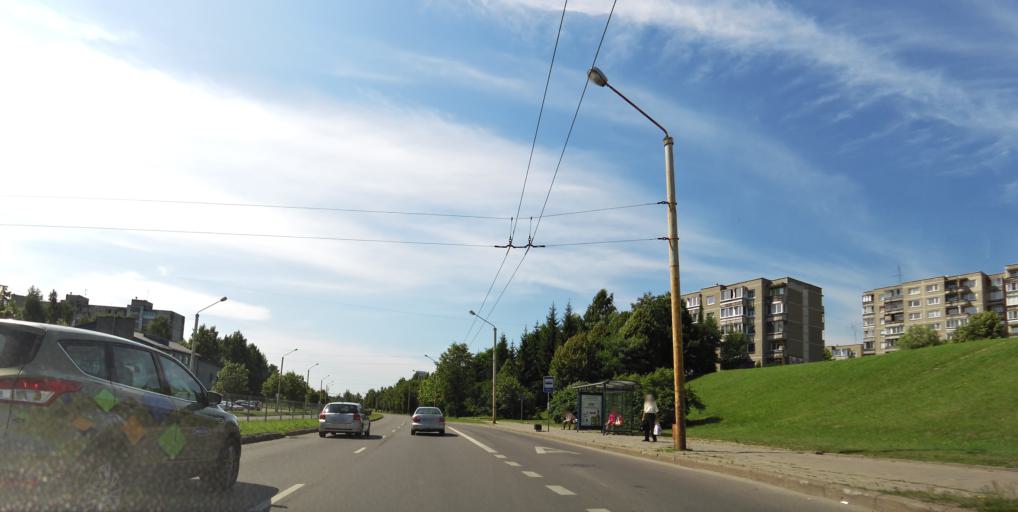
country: LT
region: Vilnius County
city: Justiniskes
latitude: 54.7111
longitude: 25.2169
